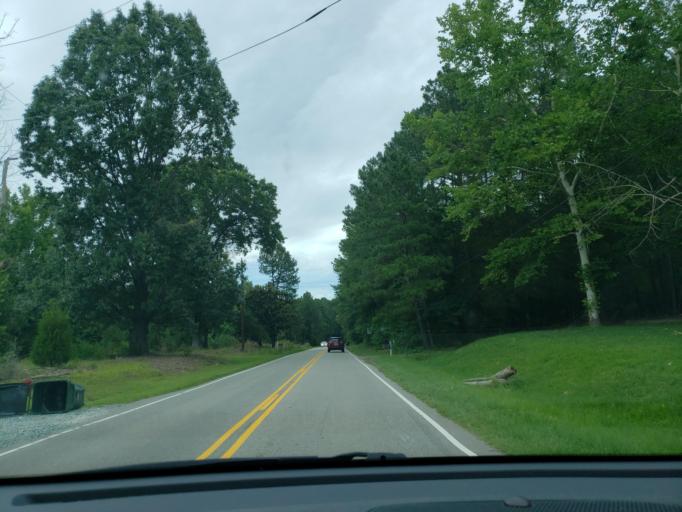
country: US
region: North Carolina
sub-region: Orange County
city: Chapel Hill
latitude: 35.8794
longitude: -78.9974
